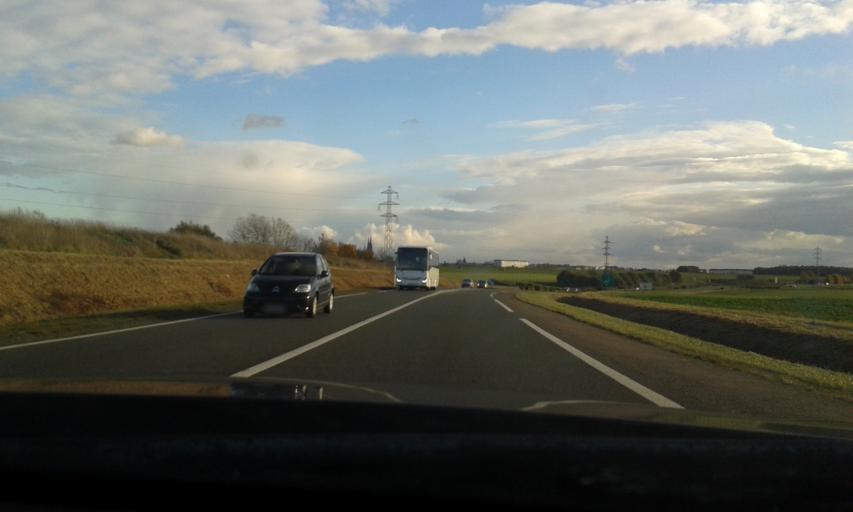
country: FR
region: Centre
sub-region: Departement d'Eure-et-Loir
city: Leves
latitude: 48.4719
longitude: 1.4637
